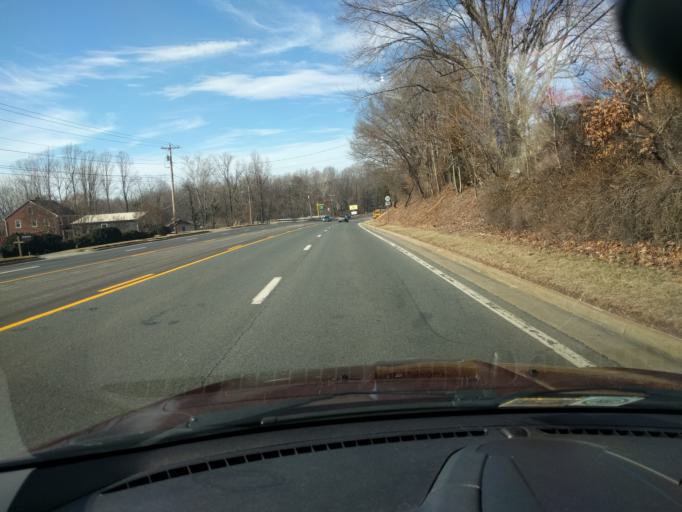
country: US
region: Virginia
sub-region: Amherst County
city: Madison Heights
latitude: 37.4861
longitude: -79.1209
